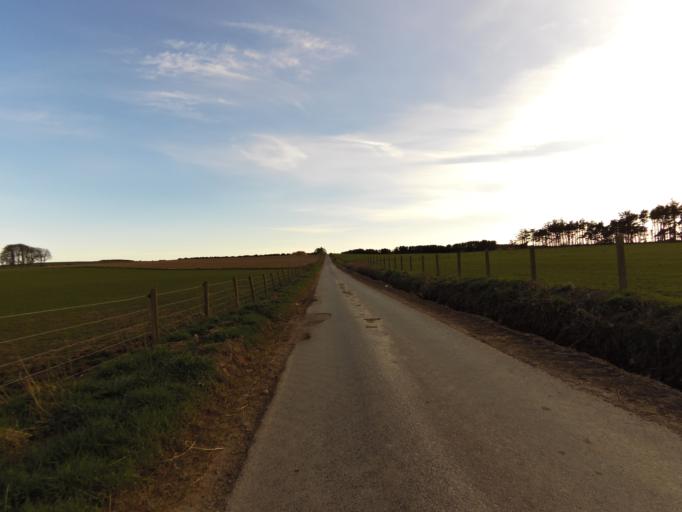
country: GB
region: Scotland
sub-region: Aberdeenshire
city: Stonehaven
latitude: 56.9423
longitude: -2.2209
